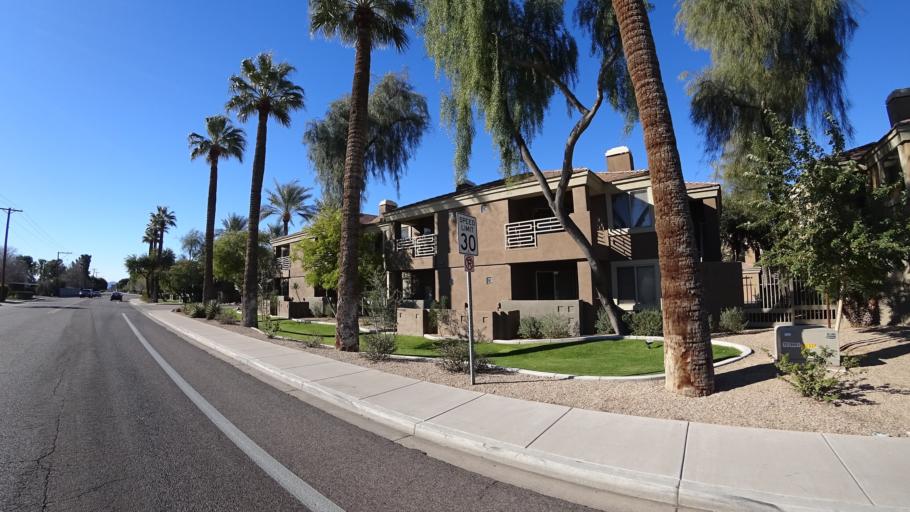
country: US
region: Arizona
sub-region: Maricopa County
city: Paradise Valley
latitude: 33.5094
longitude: -112.0041
